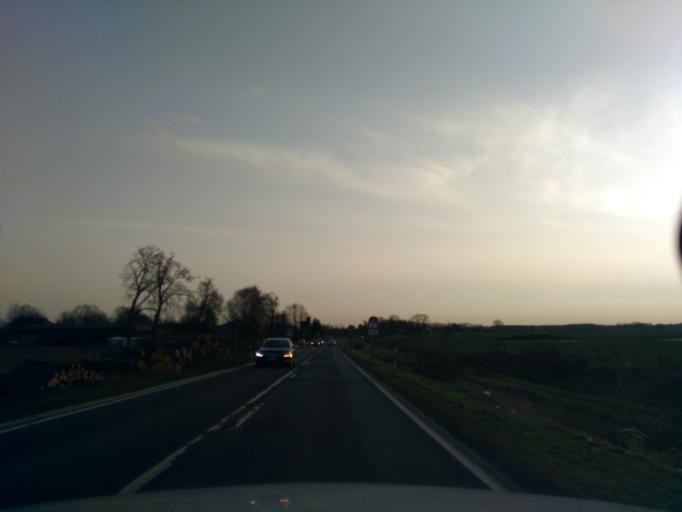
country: DE
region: Brandenburg
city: Velten
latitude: 52.7058
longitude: 13.1064
